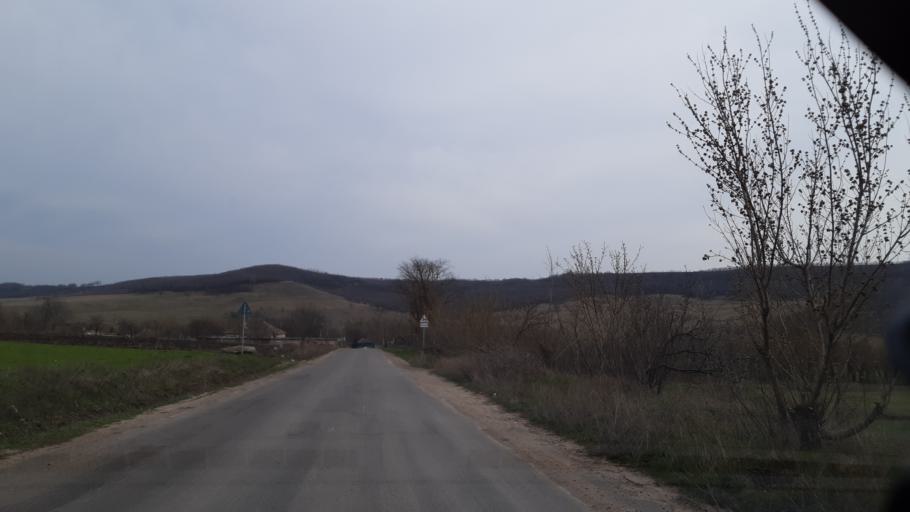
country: MD
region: Soldanesti
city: Soldanesti
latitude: 47.6879
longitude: 28.7449
